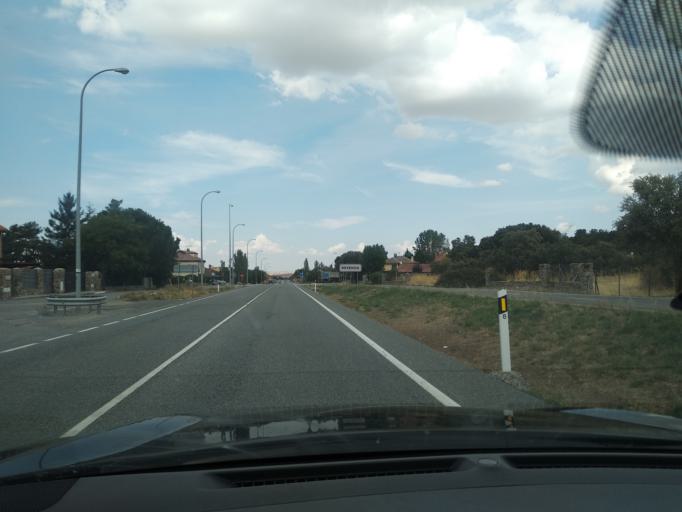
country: ES
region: Castille and Leon
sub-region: Provincia de Segovia
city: Palazuelos de Eresma
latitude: 40.8683
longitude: -4.1007
